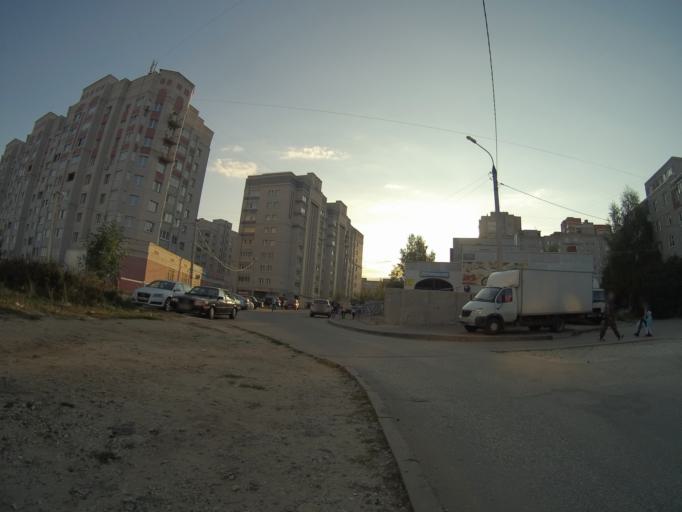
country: RU
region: Vladimir
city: Vladimir
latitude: 56.1044
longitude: 40.3523
